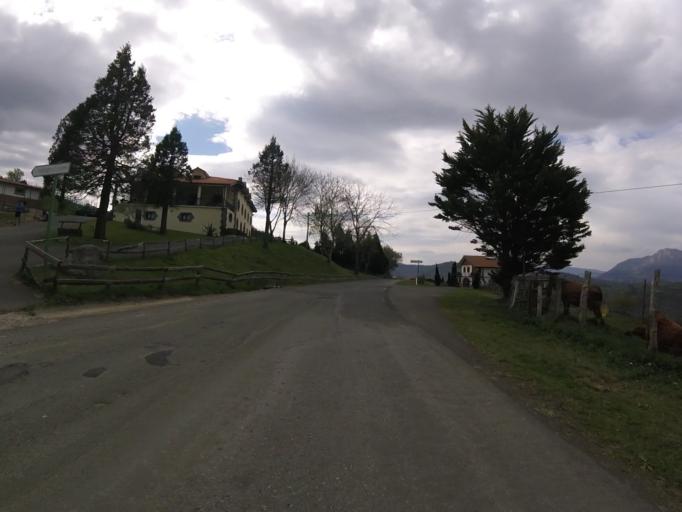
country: ES
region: Basque Country
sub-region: Provincia de Guipuzcoa
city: Aizarnazabal
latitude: 43.2516
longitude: -2.1961
